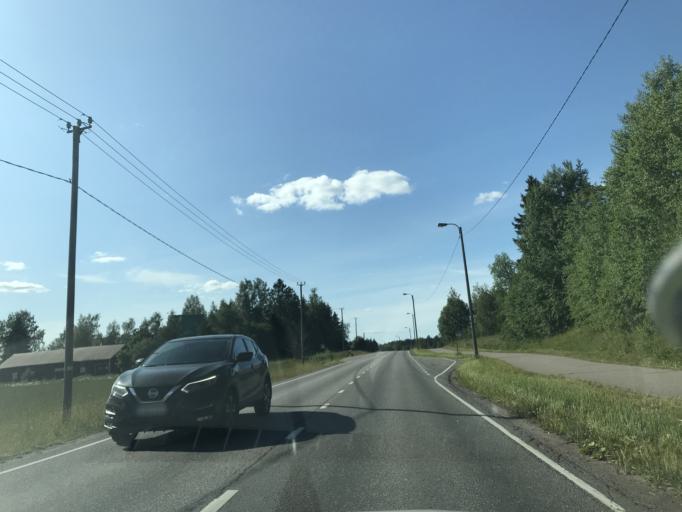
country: FI
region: Uusimaa
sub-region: Helsinki
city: Nurmijaervi
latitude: 60.3815
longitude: 24.7322
